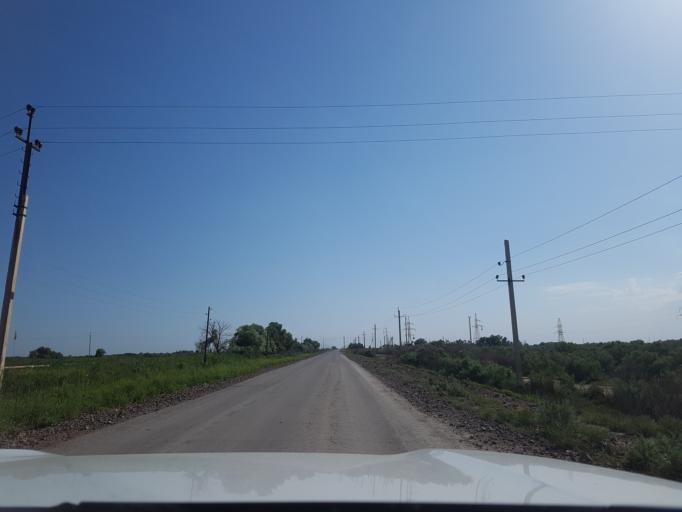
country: TM
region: Dasoguz
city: Koeneuergench
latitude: 42.0962
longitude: 58.8964
